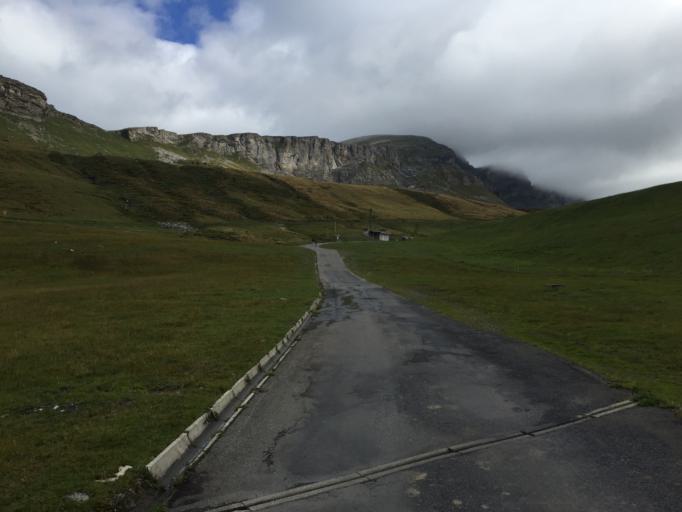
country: CH
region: Obwalden
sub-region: Obwalden
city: Engelberg
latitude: 46.7741
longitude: 8.3004
